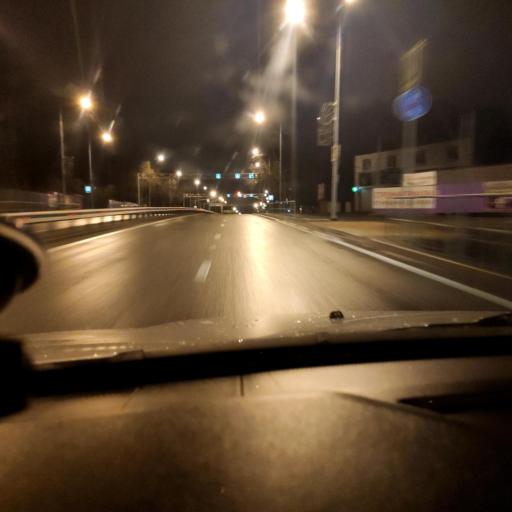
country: RU
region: Samara
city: Petra-Dubrava
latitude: 53.2972
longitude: 50.2445
